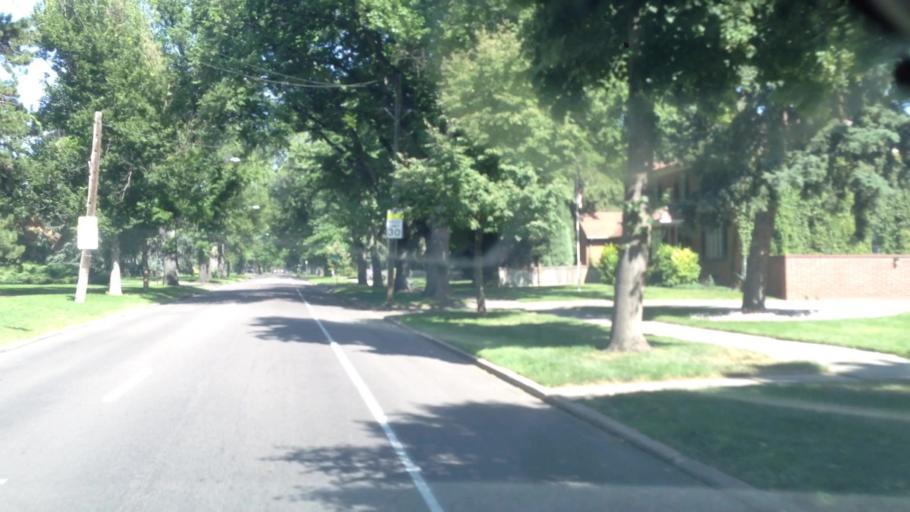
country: US
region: Colorado
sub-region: Arapahoe County
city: Glendale
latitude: 39.7434
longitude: -104.9297
